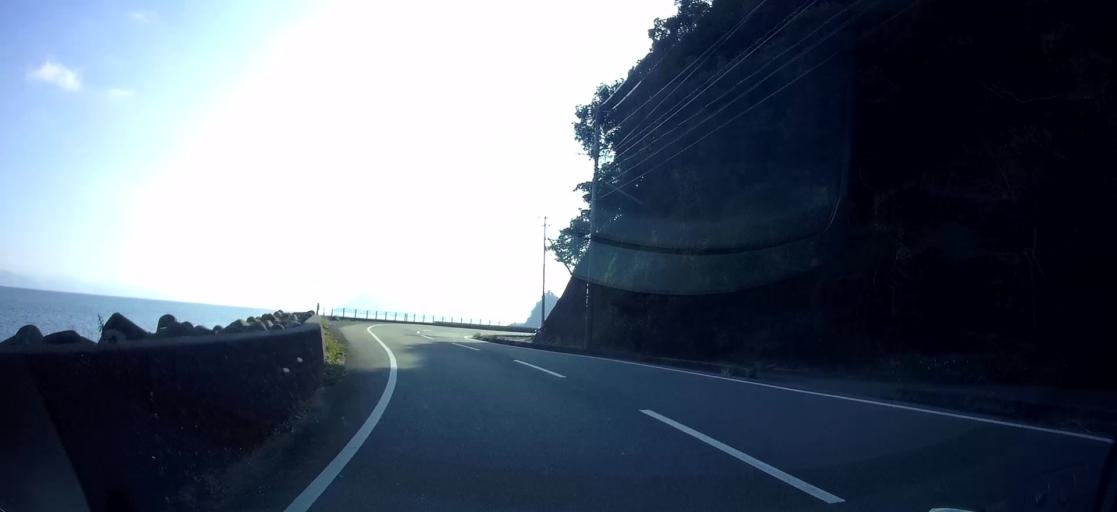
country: JP
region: Kumamoto
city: Minamata
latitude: 32.3892
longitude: 130.3857
